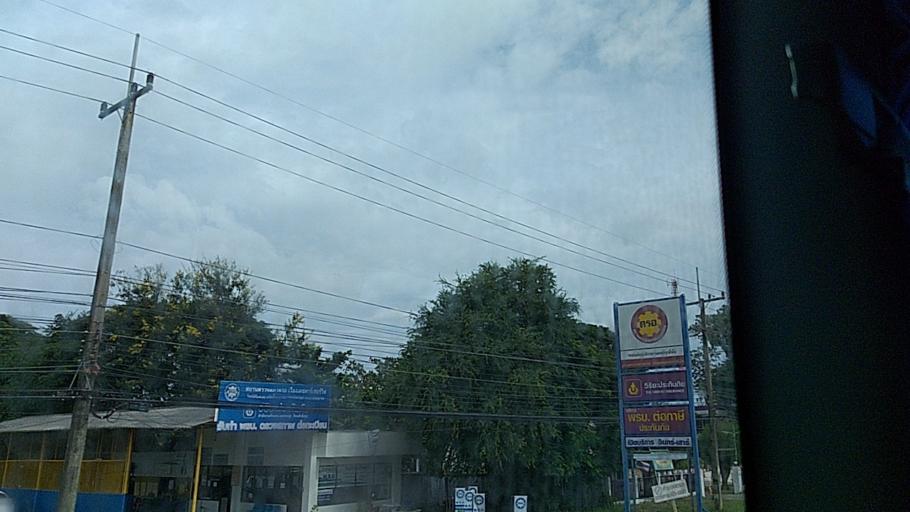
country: TH
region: Roi Et
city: Roi Et
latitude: 16.0692
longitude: 103.6049
